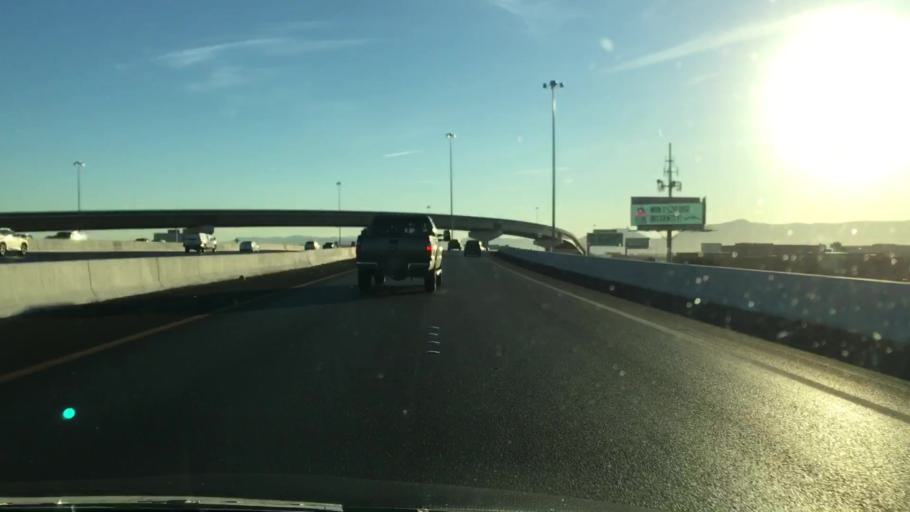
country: US
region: Nevada
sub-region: Clark County
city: Paradise
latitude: 36.0628
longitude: -115.1513
